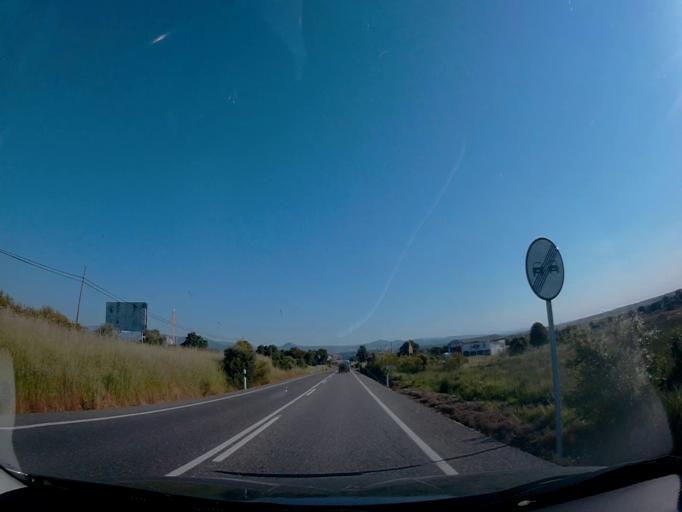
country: ES
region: Castille-La Mancha
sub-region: Province of Toledo
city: Escalona
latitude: 40.1350
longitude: -4.4044
